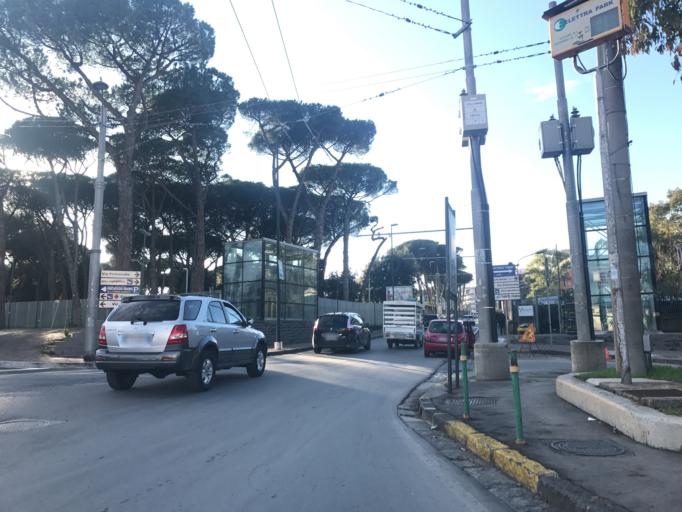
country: IT
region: Campania
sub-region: Provincia di Napoli
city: Napoli
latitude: 40.8686
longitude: 14.2280
